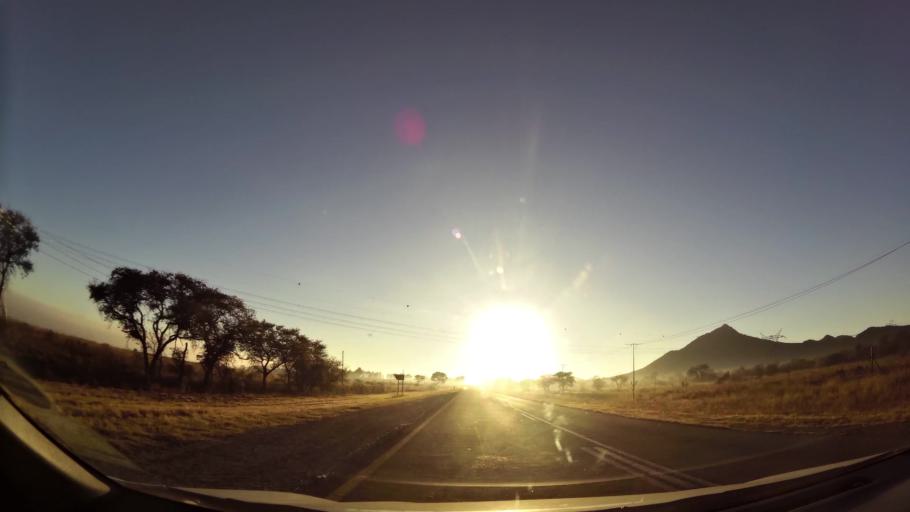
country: ZA
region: Limpopo
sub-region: Capricorn District Municipality
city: Polokwane
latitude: -24.0274
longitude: 29.2946
